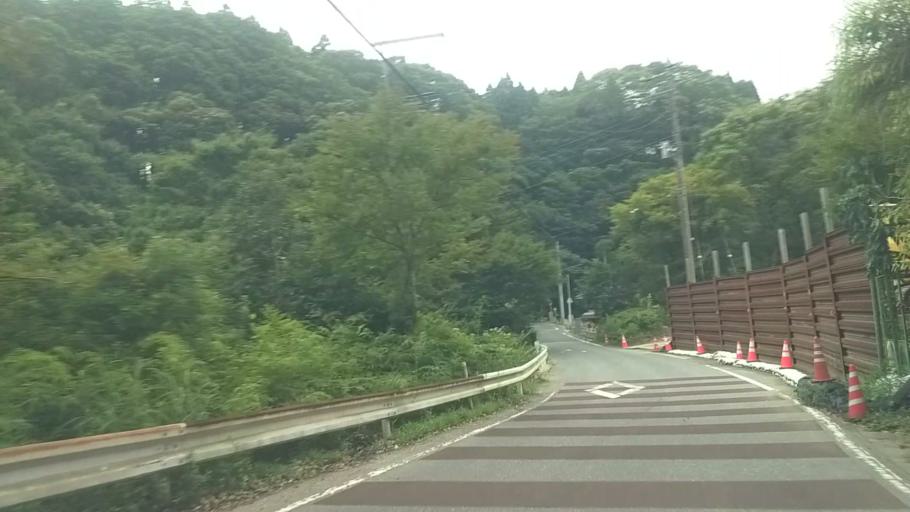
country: JP
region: Chiba
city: Kawaguchi
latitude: 35.2277
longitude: 140.1282
